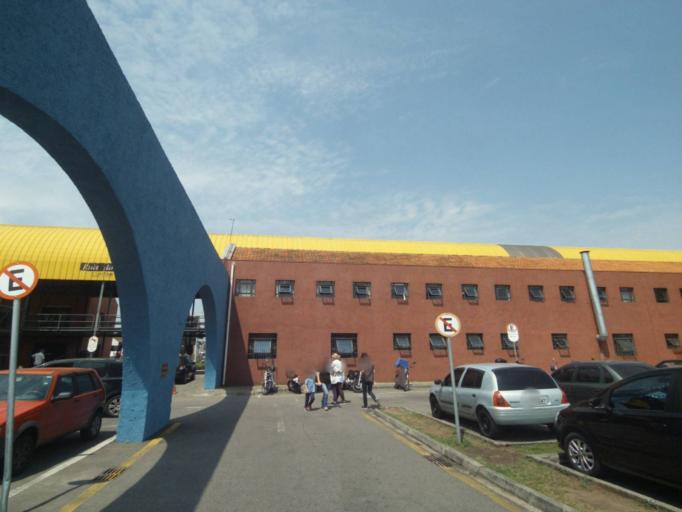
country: BR
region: Parana
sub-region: Curitiba
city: Curitiba
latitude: -25.4778
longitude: -49.3268
